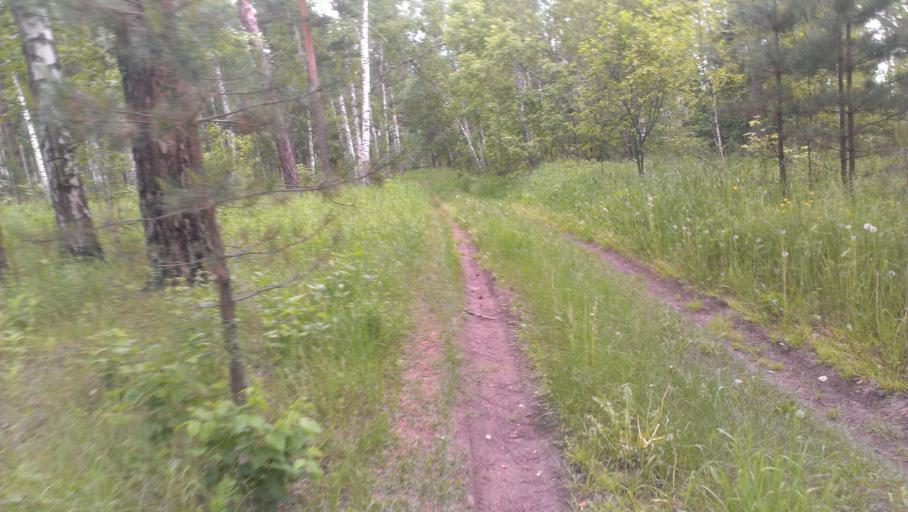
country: RU
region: Altai Krai
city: Sannikovo
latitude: 53.3390
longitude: 84.0497
